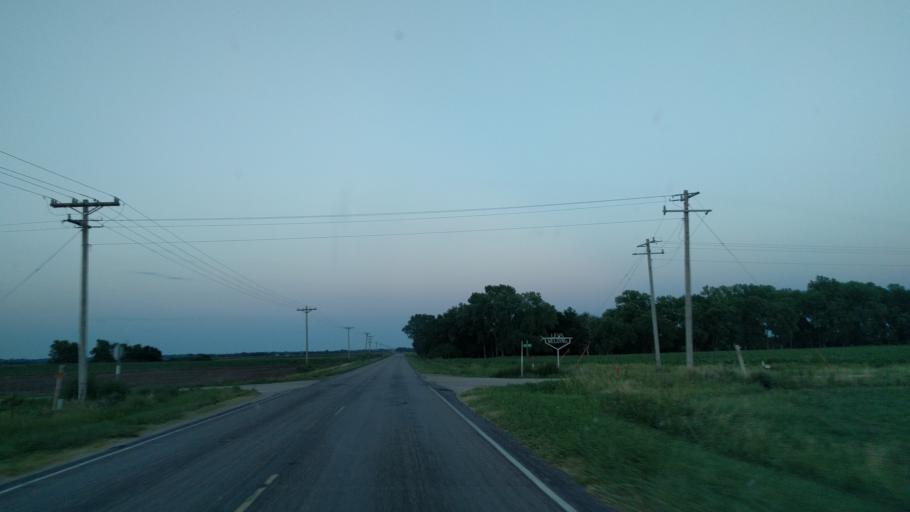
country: US
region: Kansas
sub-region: Reno County
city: Nickerson
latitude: 38.2176
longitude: -98.1068
